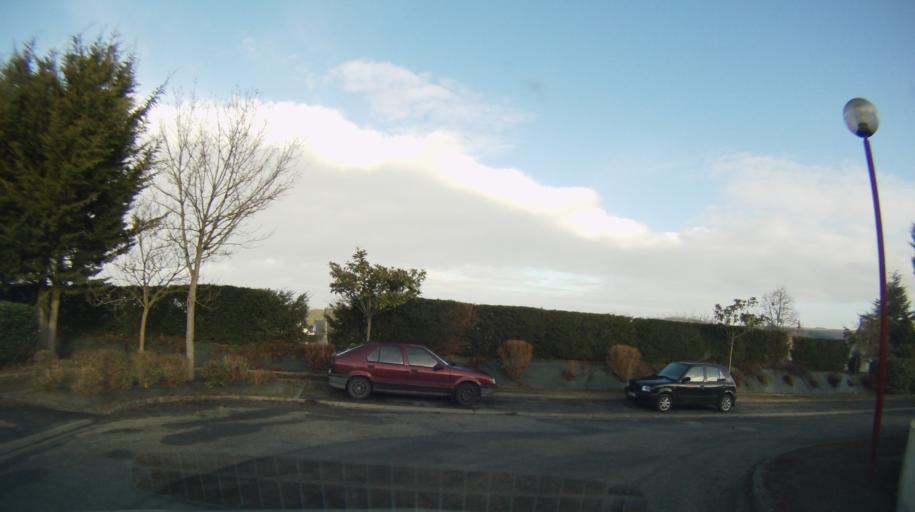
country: FR
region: Brittany
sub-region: Departement d'Ille-et-Vilaine
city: Janze
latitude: 47.9510
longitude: -1.5409
